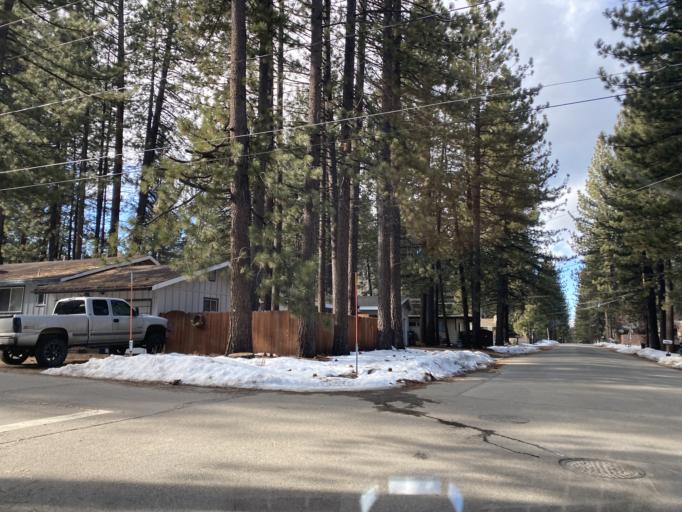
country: US
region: California
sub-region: El Dorado County
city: South Lake Tahoe
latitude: 38.9206
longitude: -119.9786
